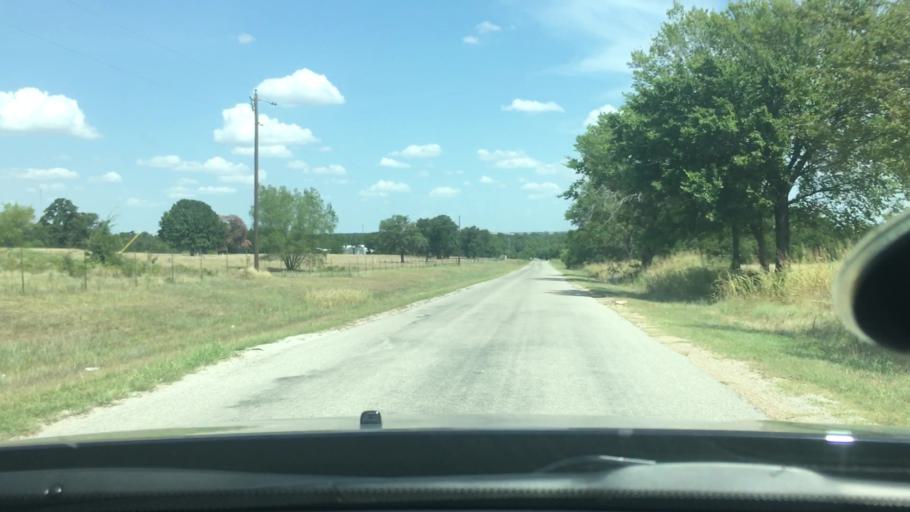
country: US
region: Oklahoma
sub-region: Carter County
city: Ardmore
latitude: 34.0496
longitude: -97.1957
